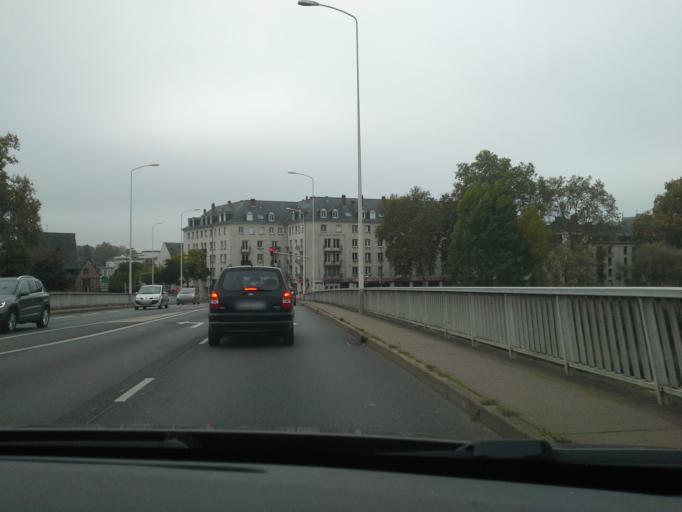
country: FR
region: Centre
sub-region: Departement d'Indre-et-Loire
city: Tours
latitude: 47.3986
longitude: 0.6998
